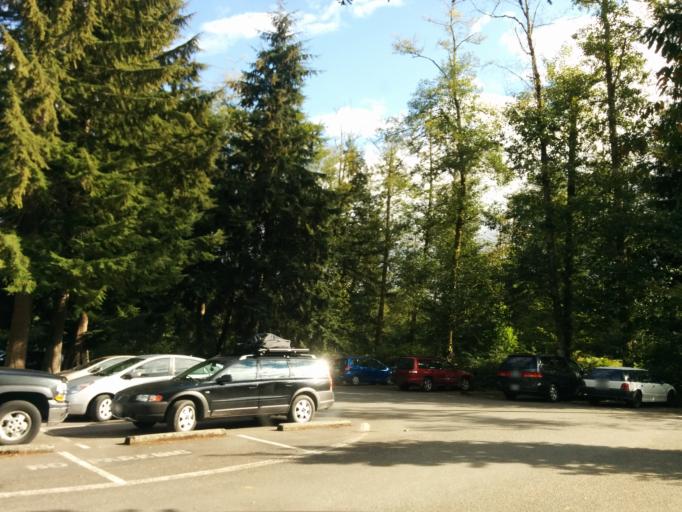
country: US
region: Washington
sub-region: Snohomish County
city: Gold Bar
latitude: 47.8672
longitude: -121.6787
